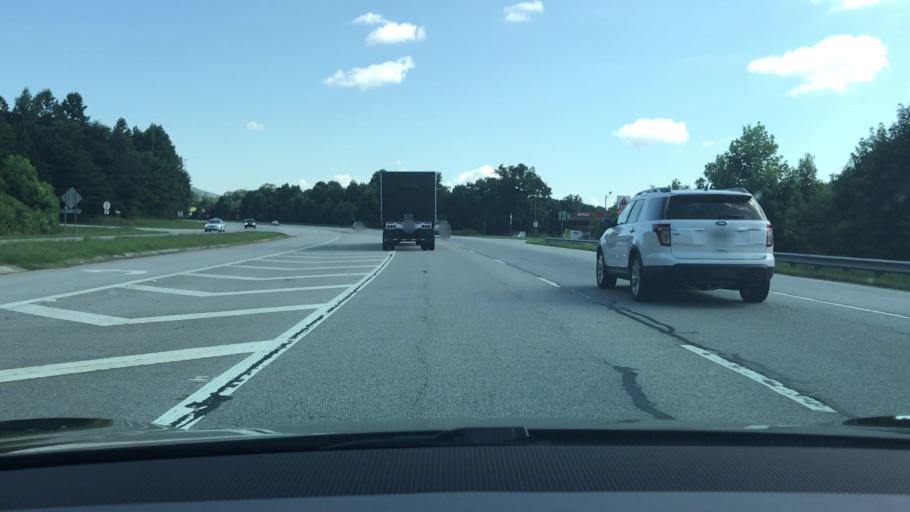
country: US
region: Georgia
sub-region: Habersham County
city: Clarkesville
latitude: 34.6773
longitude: -83.4259
